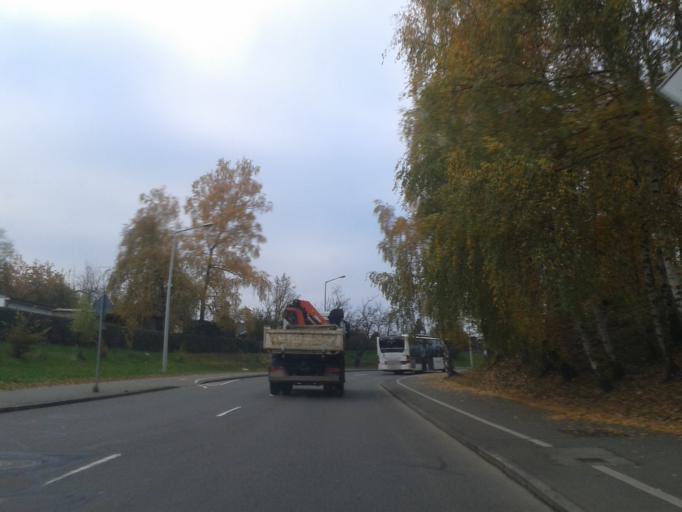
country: DE
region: Saxony
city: Freiberg
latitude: 50.9068
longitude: 13.3495
